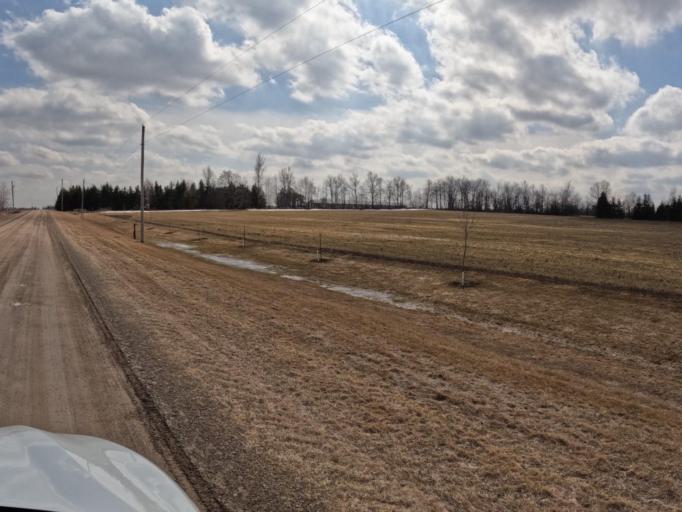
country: CA
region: Ontario
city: Shelburne
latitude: 43.9771
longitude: -80.2685
